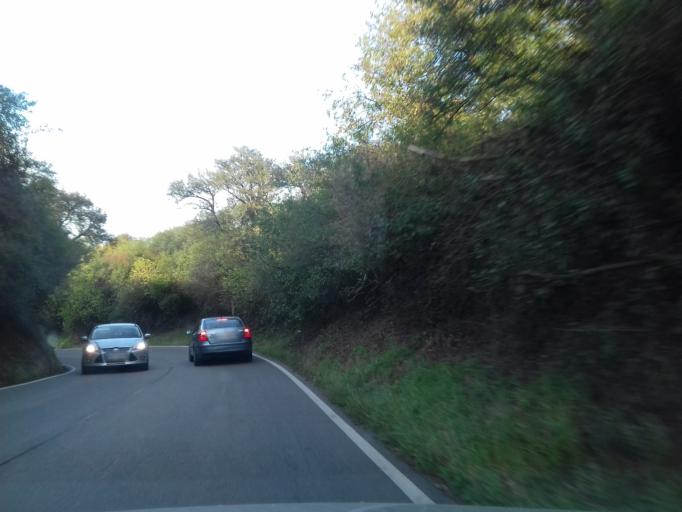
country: CZ
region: Central Bohemia
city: Kamenny Privoz
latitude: 49.8717
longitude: 14.5040
